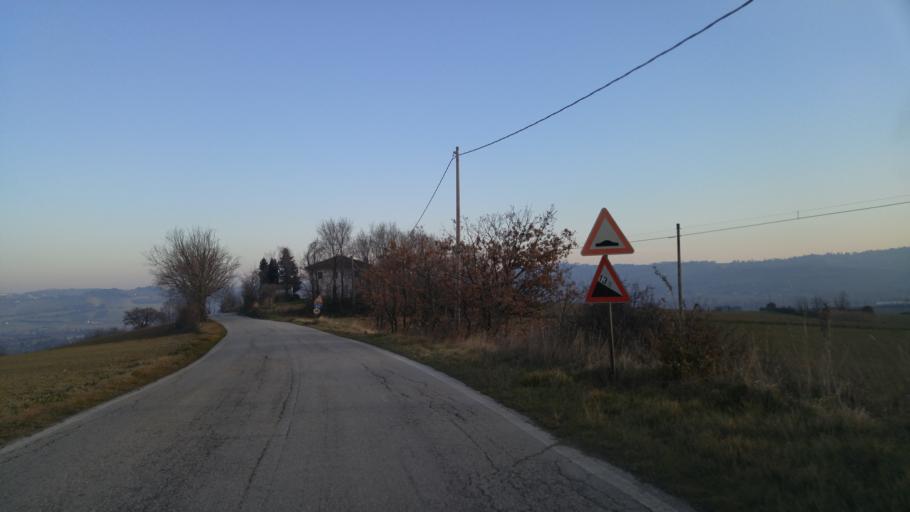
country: IT
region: The Marches
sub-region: Provincia di Pesaro e Urbino
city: Monte Porzio
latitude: 43.6949
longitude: 13.0327
